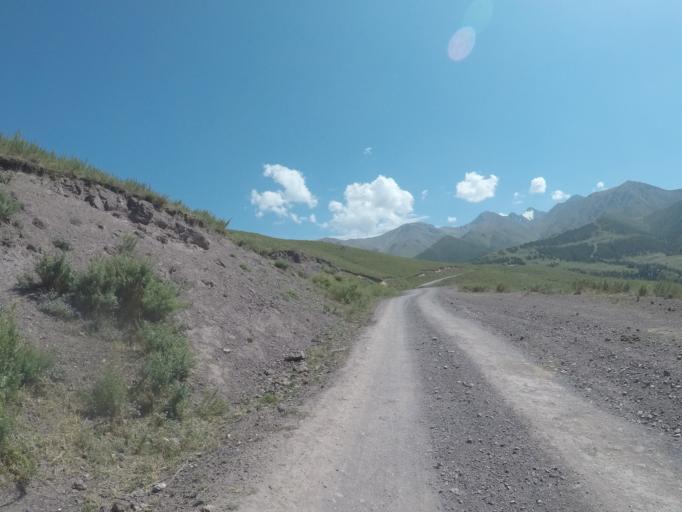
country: KG
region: Chuy
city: Bishkek
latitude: 42.6507
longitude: 74.5201
